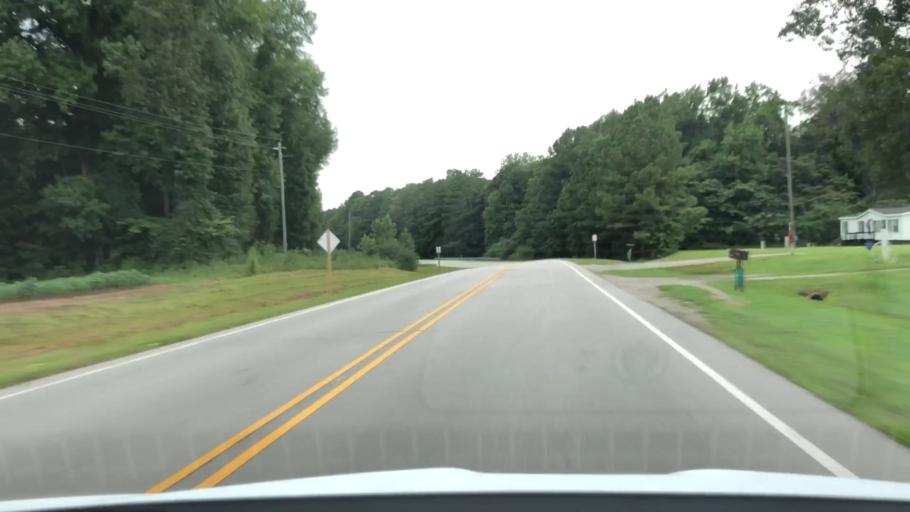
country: US
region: North Carolina
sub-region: Jones County
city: Trenton
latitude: 35.0322
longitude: -77.3167
